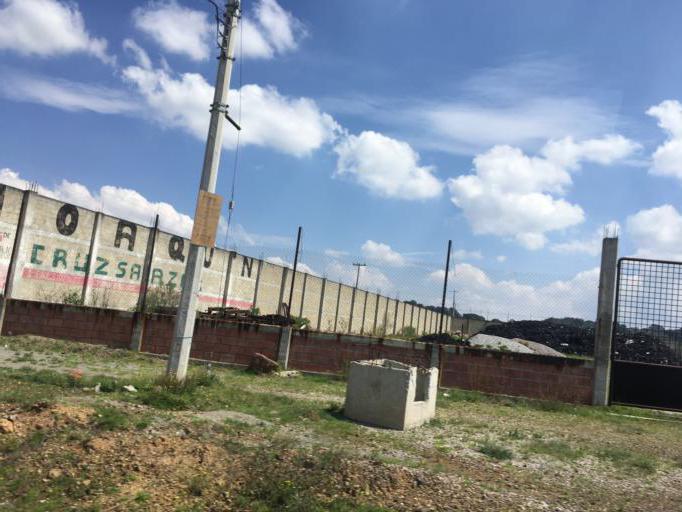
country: MX
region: Mexico
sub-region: Jilotepec
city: Octeyuco Dos Mil
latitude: 19.8865
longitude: -99.6466
